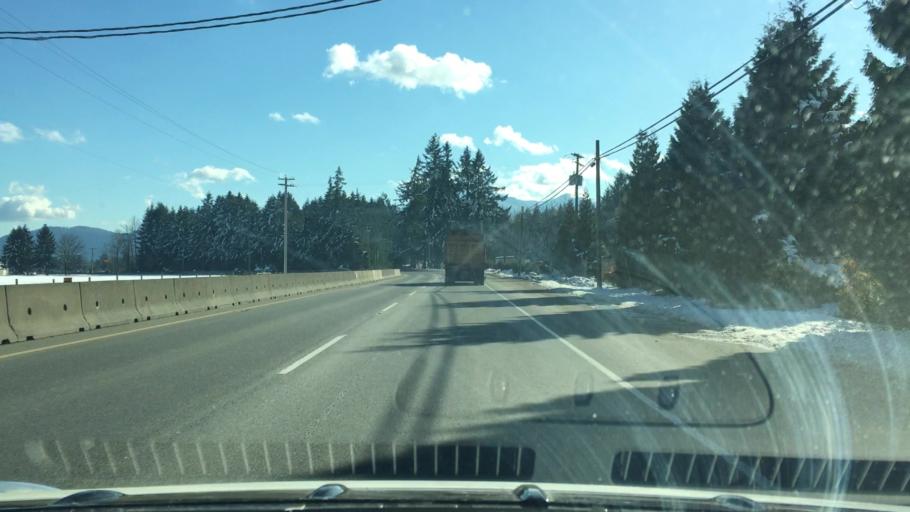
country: CA
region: British Columbia
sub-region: Cowichan Valley Regional District
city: Ladysmith
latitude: 49.0509
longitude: -123.8775
